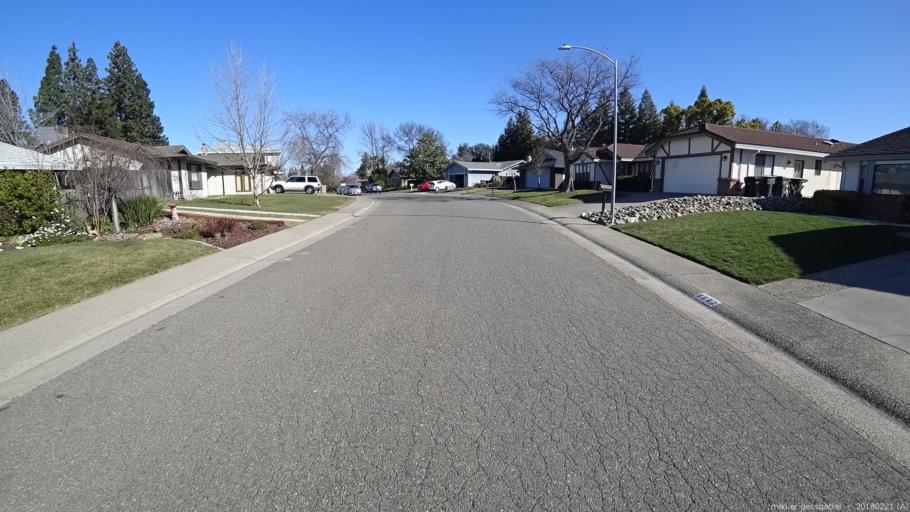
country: US
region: California
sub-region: Sacramento County
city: Orangevale
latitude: 38.6833
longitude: -121.2369
